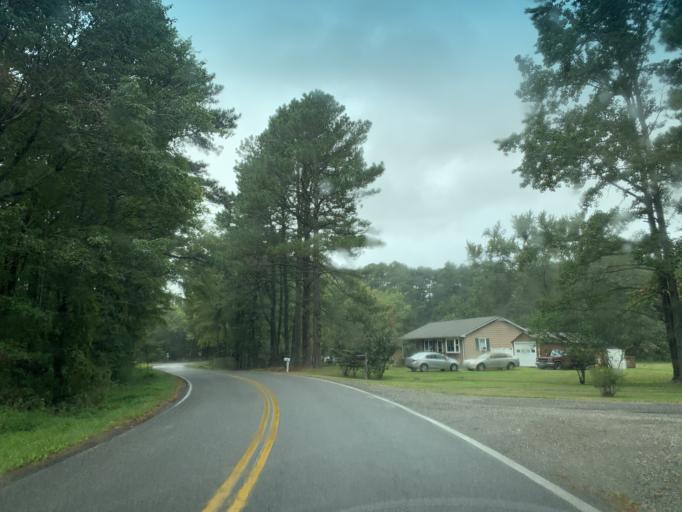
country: US
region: Maryland
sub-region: Caroline County
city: Ridgely
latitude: 38.9173
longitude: -75.8627
